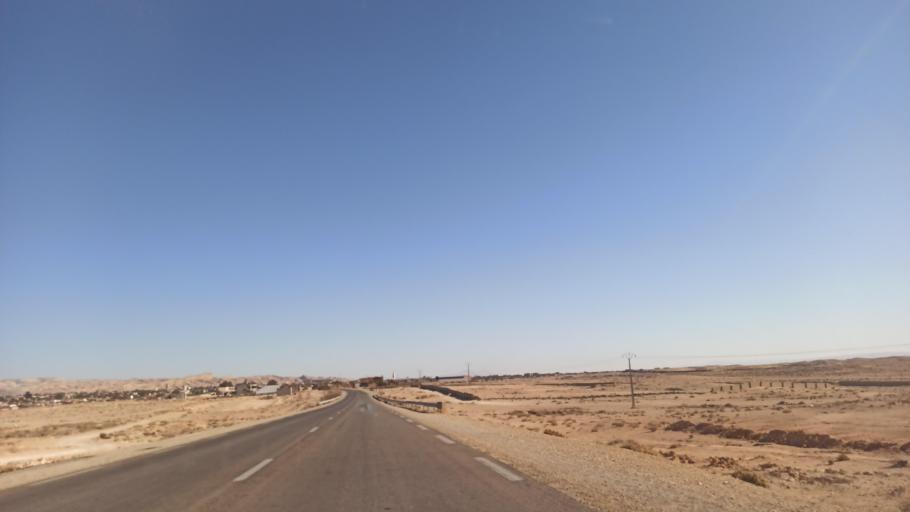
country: TN
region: Gafsa
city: Al Metlaoui
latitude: 34.3072
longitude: 8.3701
